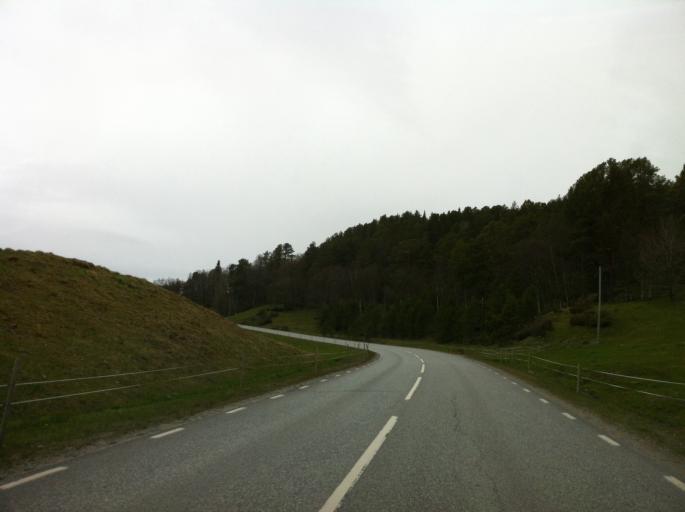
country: NO
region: Sor-Trondelag
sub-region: Tydal
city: Aas
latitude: 62.6157
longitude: 12.4884
